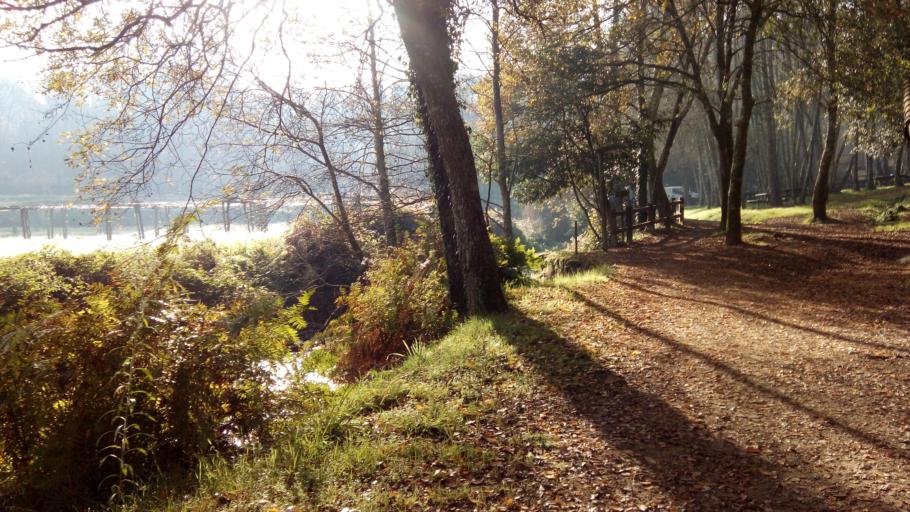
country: ES
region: Galicia
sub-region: Provincia de Pontevedra
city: Meis
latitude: 42.4910
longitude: -8.7522
